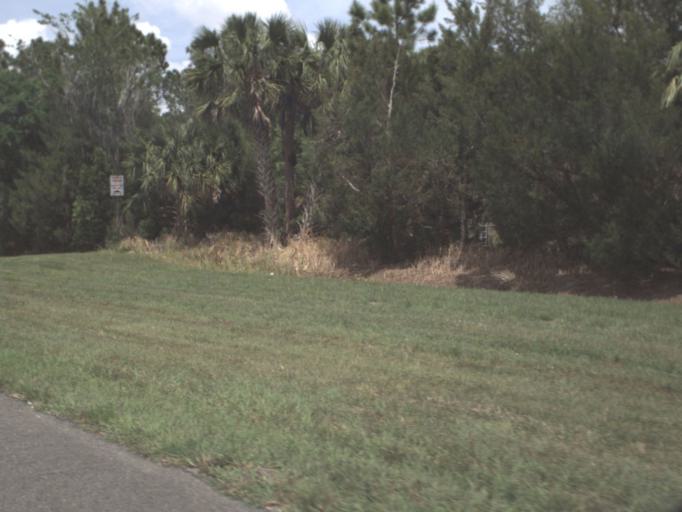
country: US
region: Florida
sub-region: Flagler County
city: Bunnell
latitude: 29.3396
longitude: -81.3108
